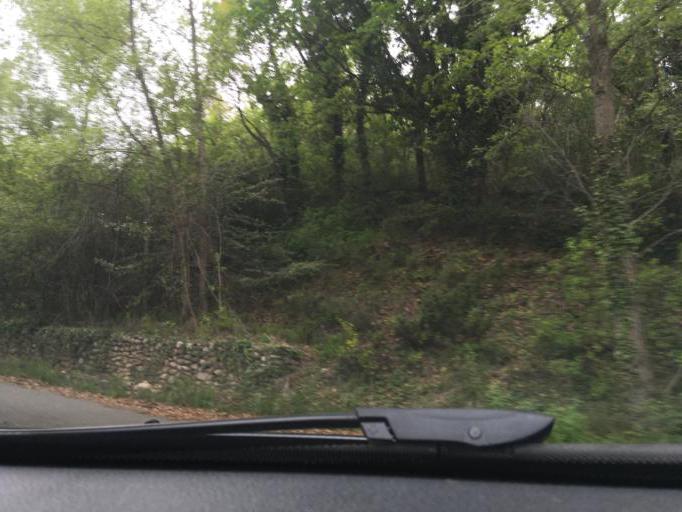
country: FR
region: Provence-Alpes-Cote d'Azur
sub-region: Departement des Alpes-de-Haute-Provence
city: Riez
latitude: 43.7621
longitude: 6.1521
